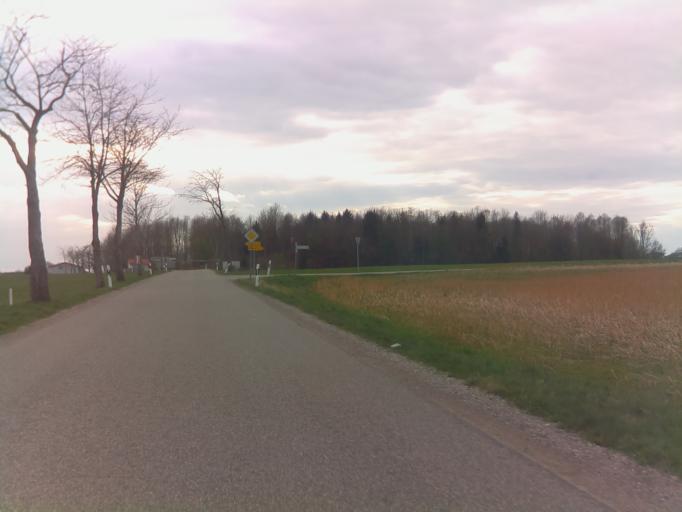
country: DE
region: Bavaria
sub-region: Upper Bavaria
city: Purgen
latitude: 48.0059
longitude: 10.9213
